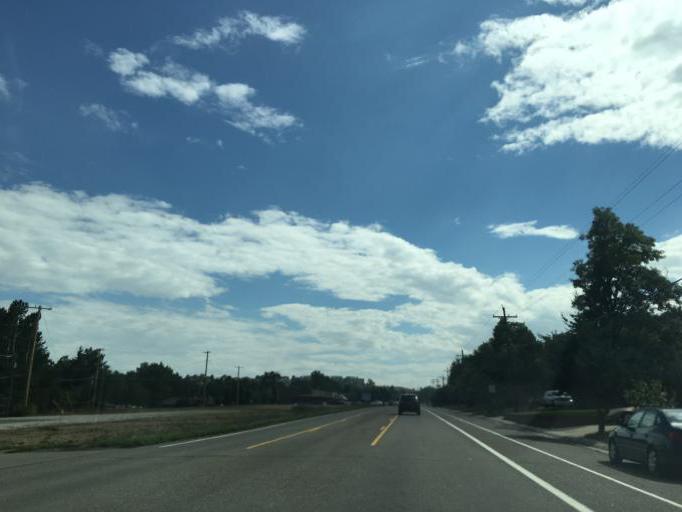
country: US
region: Colorado
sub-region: Jefferson County
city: Applewood
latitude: 39.7504
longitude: -105.1424
